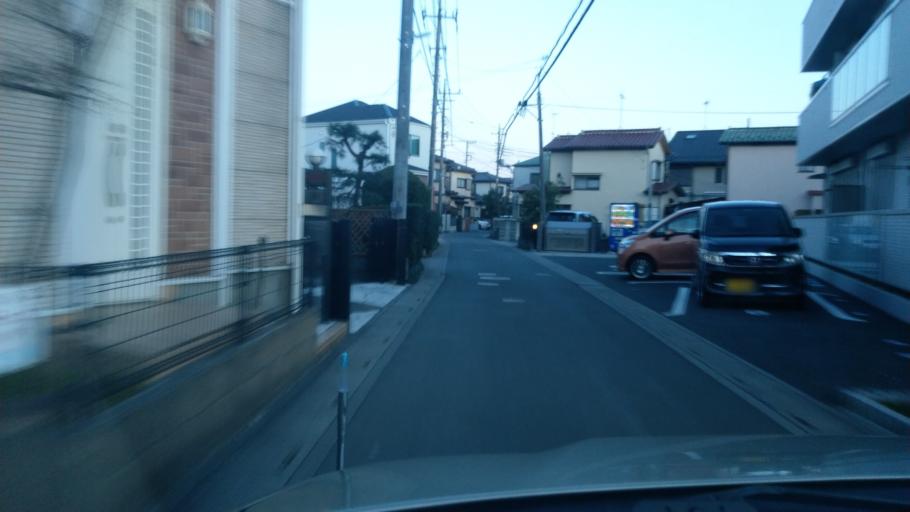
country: JP
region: Saitama
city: Yono
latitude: 35.9179
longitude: 139.5833
